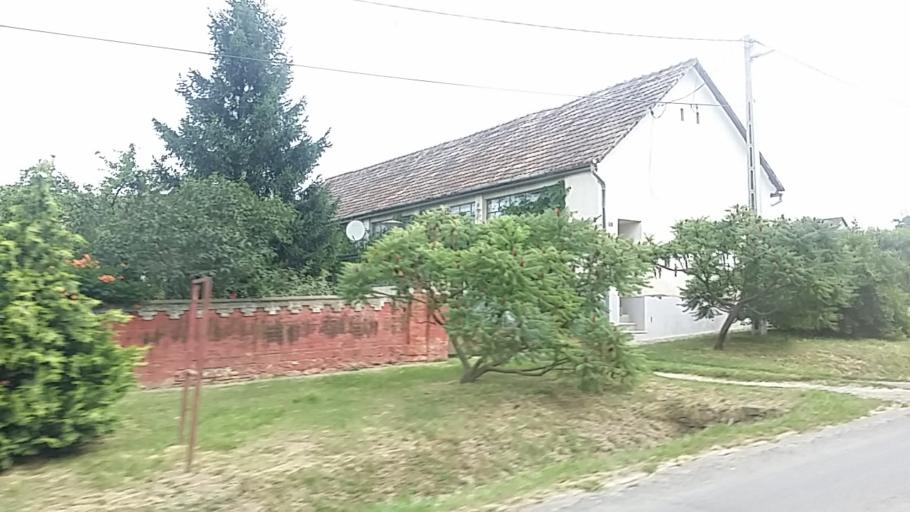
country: HU
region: Baranya
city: Boly
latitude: 45.9369
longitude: 18.4736
